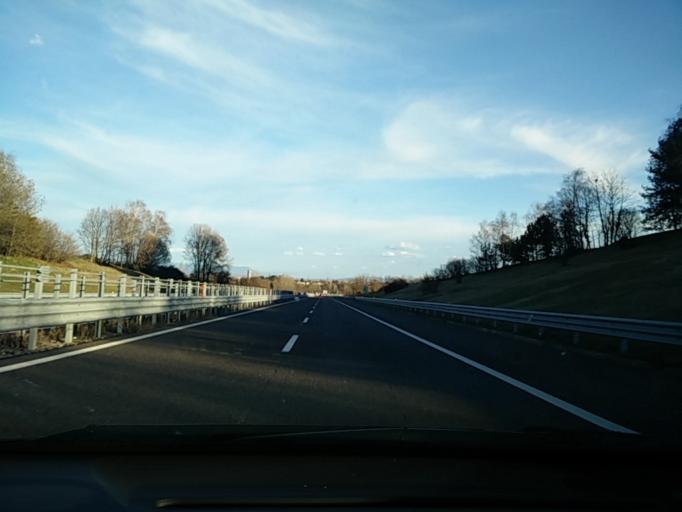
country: IT
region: Friuli Venezia Giulia
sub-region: Provincia di Udine
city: Pagnacco
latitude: 46.1312
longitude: 13.1924
